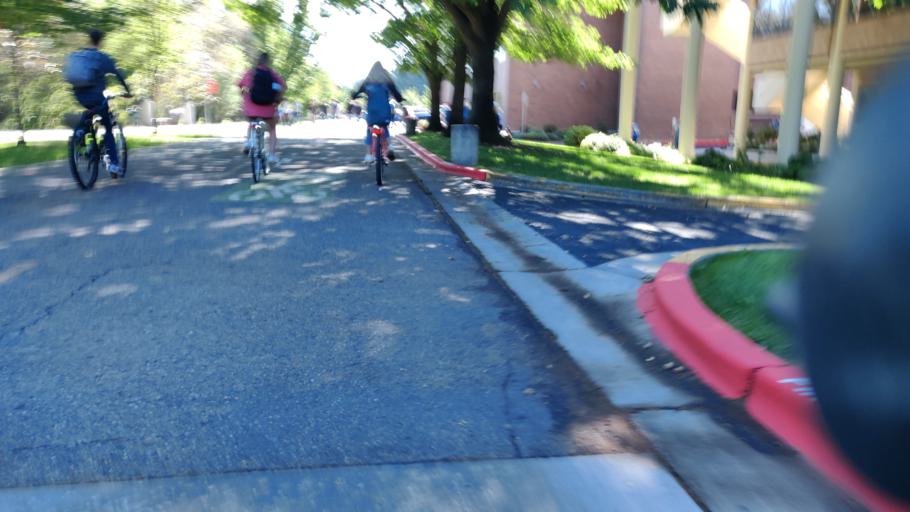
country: US
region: Idaho
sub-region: Ada County
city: Boise
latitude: 43.6067
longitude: -116.2067
